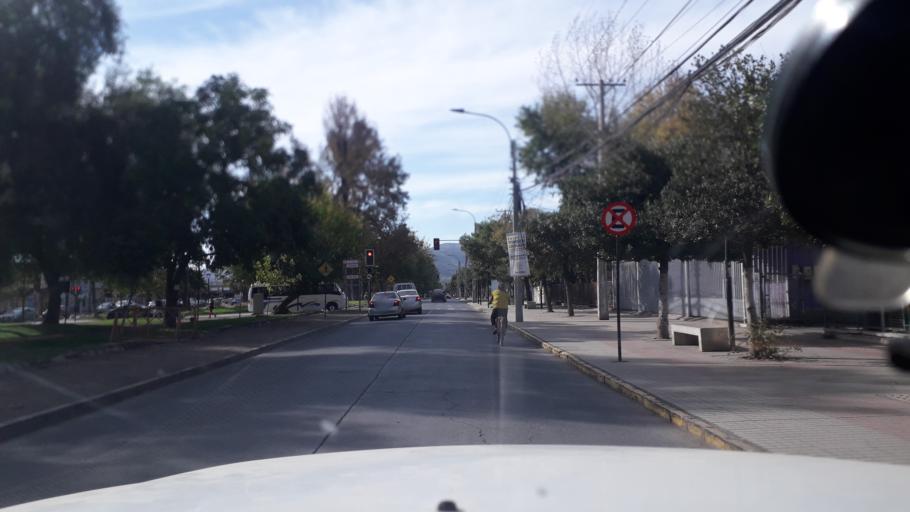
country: CL
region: Valparaiso
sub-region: Provincia de San Felipe
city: San Felipe
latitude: -32.7542
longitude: -70.7209
